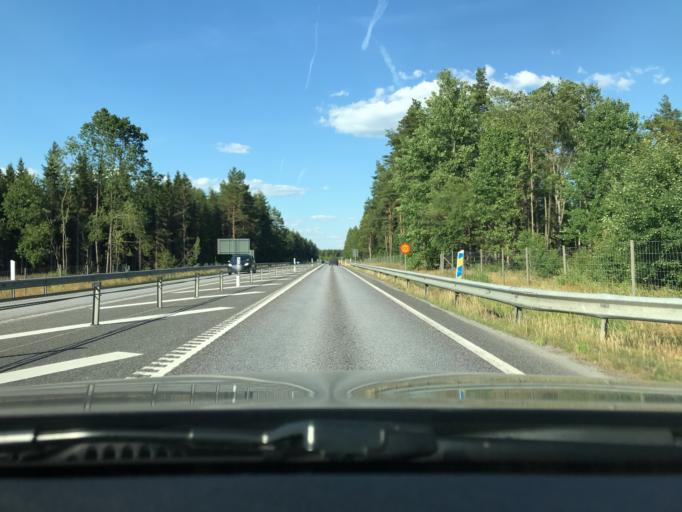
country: SE
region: Kronoberg
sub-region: Alvesta Kommun
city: Vislanda
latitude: 56.6874
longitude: 14.3230
